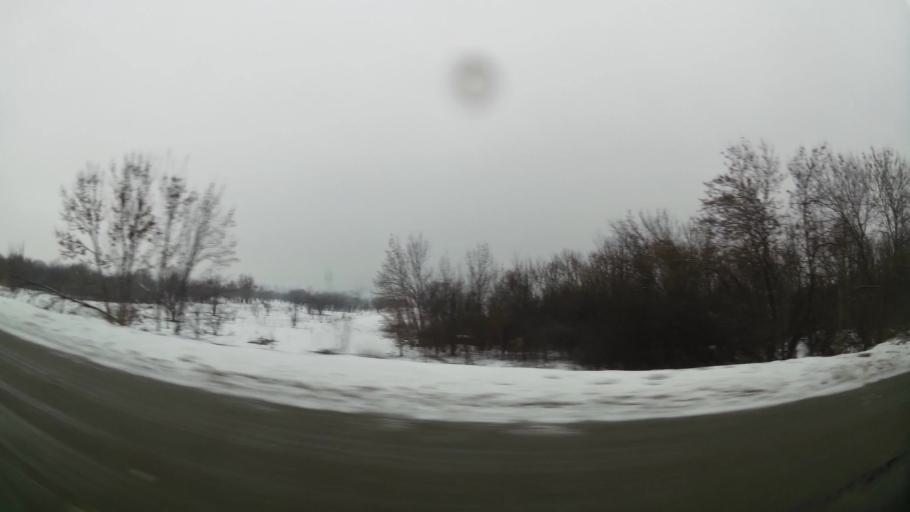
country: RS
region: Central Serbia
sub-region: Belgrade
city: Cukarica
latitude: 44.7598
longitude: 20.3865
